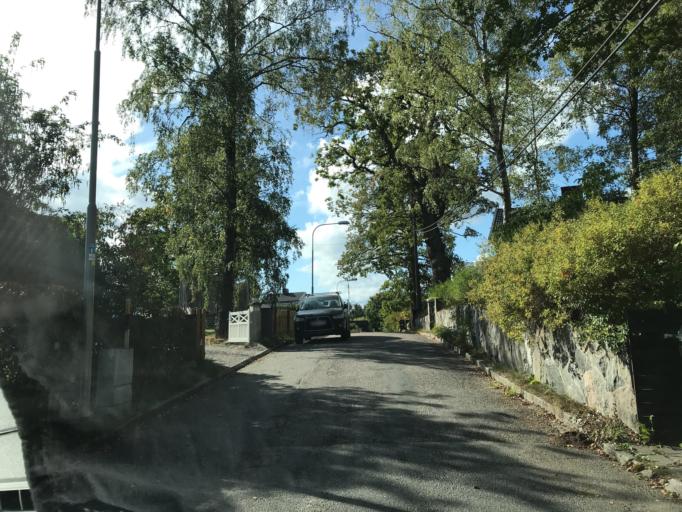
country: SE
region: Stockholm
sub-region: Huddinge Kommun
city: Segeltorp
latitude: 59.2746
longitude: 17.9585
